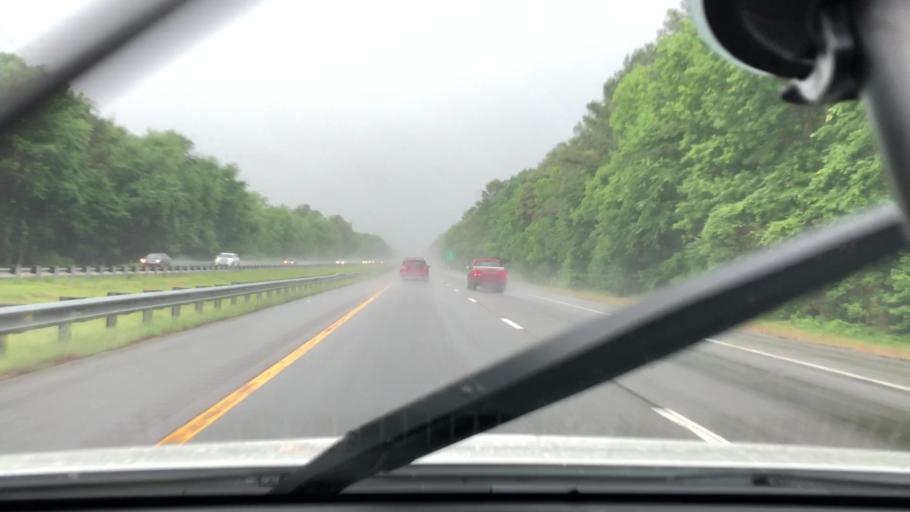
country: US
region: North Carolina
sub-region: Halifax County
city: Halifax
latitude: 36.3359
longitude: -77.6955
